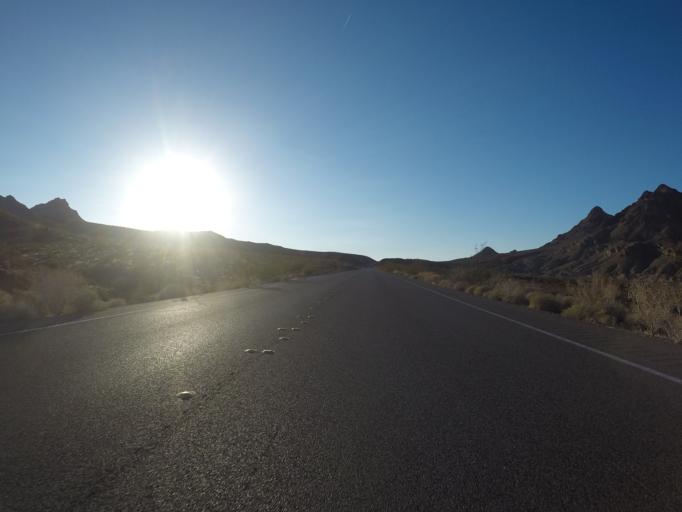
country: US
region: Nevada
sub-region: Clark County
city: Moapa Valley
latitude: 36.2444
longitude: -114.4993
